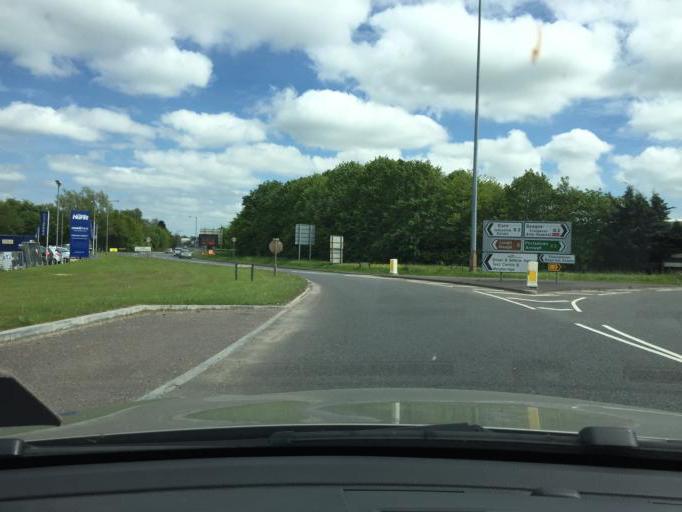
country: GB
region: Northern Ireland
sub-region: Armagh District
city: Portadown
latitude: 54.4486
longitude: -6.4252
